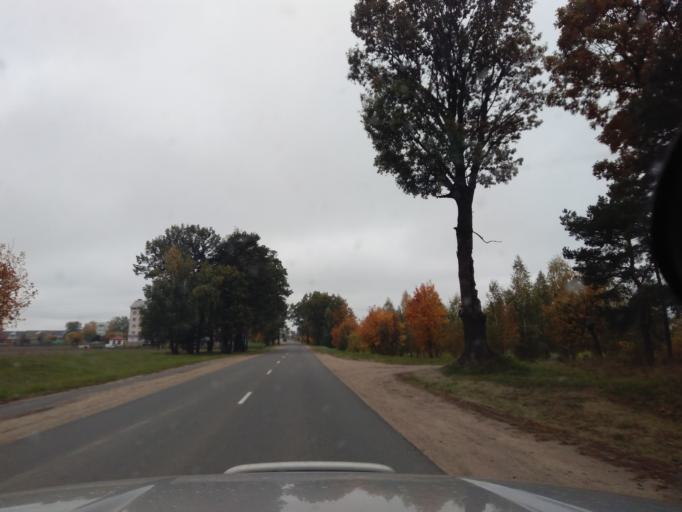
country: BY
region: Minsk
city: Kapyl'
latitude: 53.1494
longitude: 27.1214
